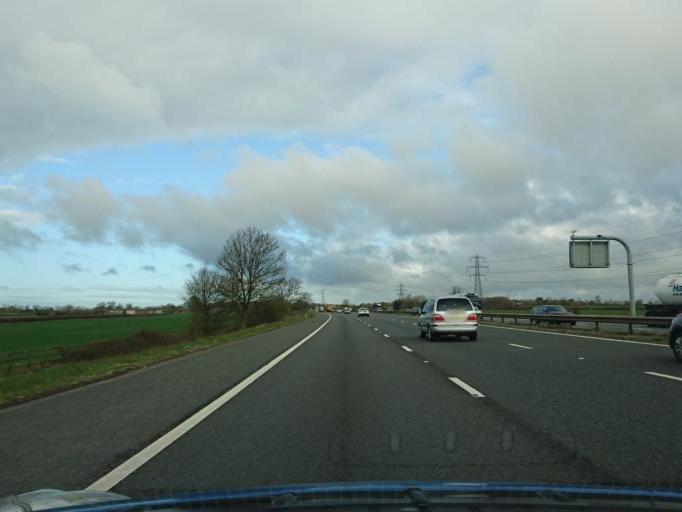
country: GB
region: England
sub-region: Wiltshire
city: Lydiard Tregoze
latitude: 51.5533
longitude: -1.8736
